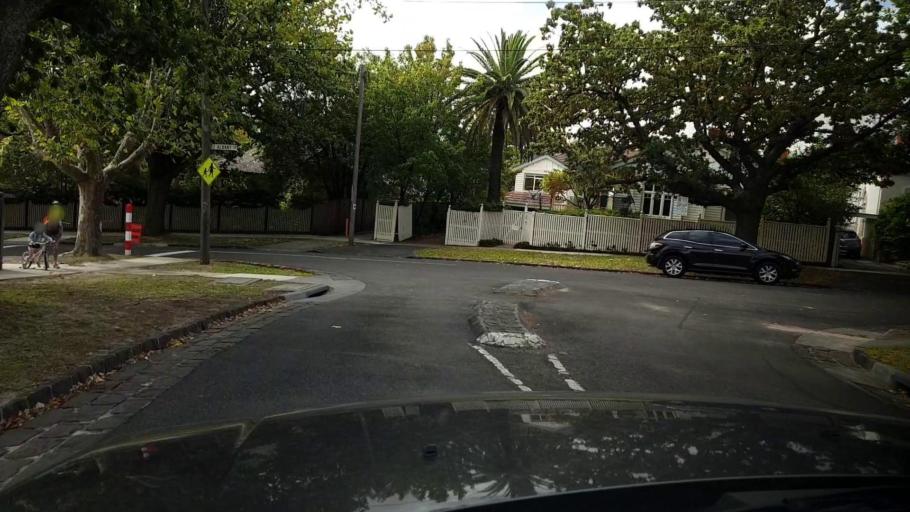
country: AU
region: Victoria
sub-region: Whitehorse
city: Surrey Hills
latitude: -37.8247
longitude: 145.1022
